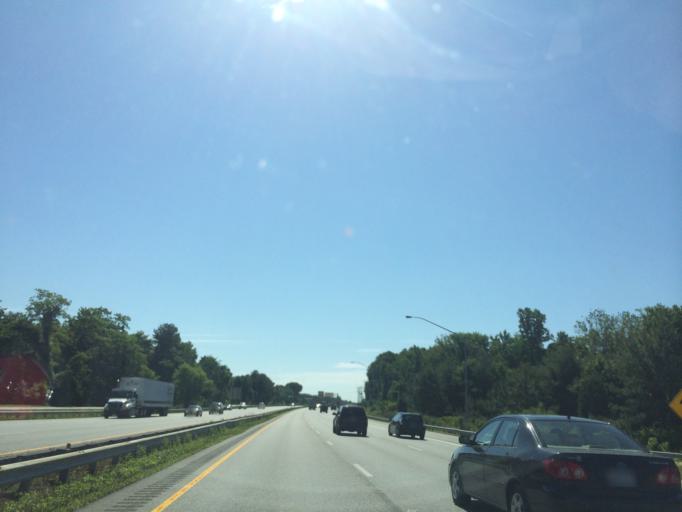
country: US
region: Maryland
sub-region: Anne Arundel County
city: Cape Saint Claire
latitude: 39.0260
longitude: -76.4396
